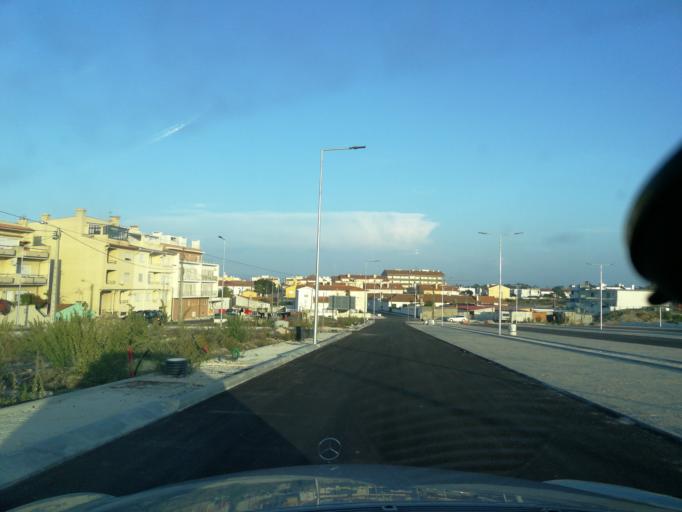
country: PT
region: Aveiro
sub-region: Murtosa
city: Murtosa
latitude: 40.7589
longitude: -8.7126
